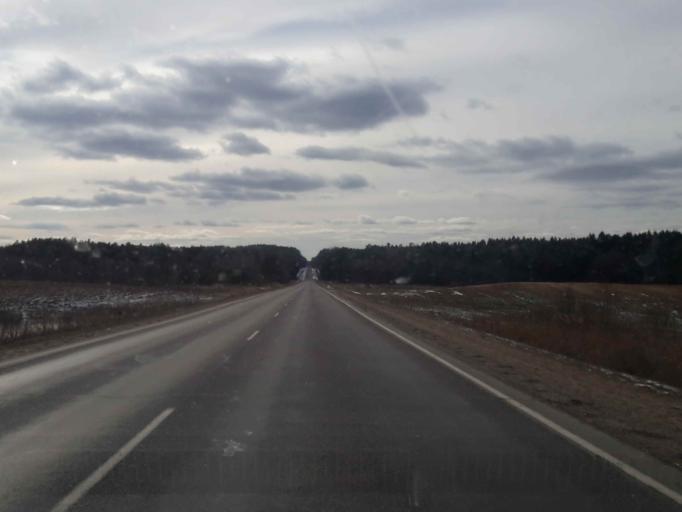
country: BY
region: Vitebsk
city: Pastavy
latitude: 55.0215
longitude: 26.9221
